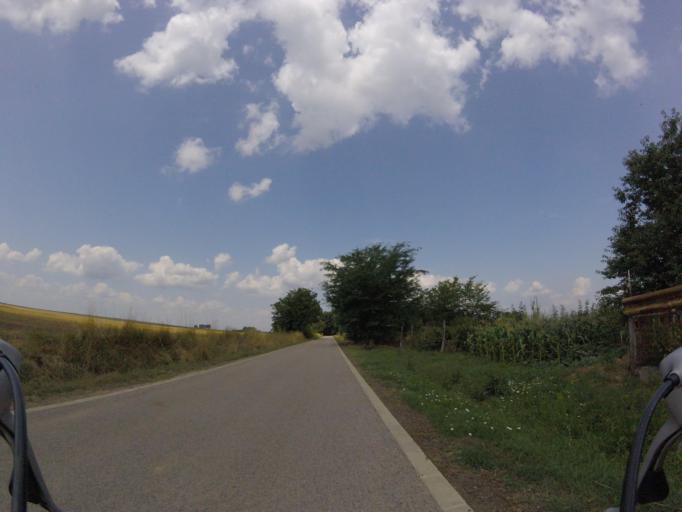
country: SK
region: Nitriansky
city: Sahy
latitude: 48.0419
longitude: 18.9047
